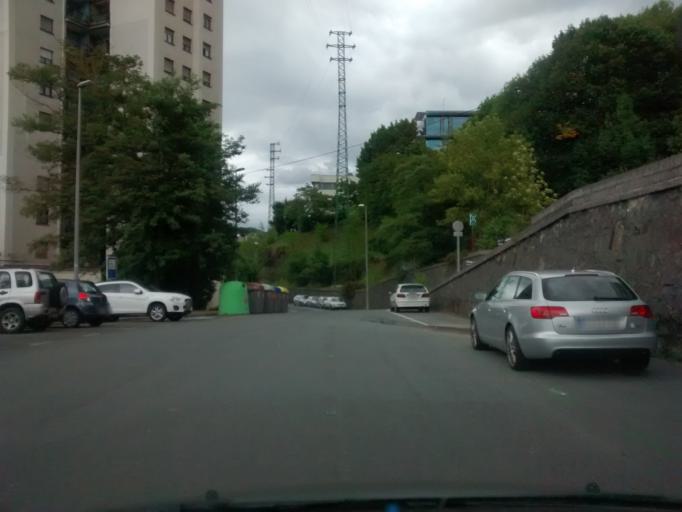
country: ES
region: Basque Country
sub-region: Provincia de Guipuzcoa
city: Arrasate / Mondragon
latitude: 43.0606
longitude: -2.5012
